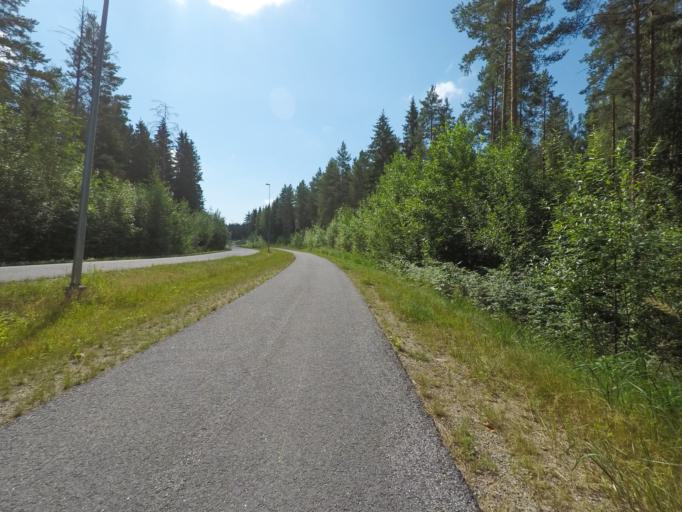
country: FI
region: Southern Savonia
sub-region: Mikkeli
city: Puumala
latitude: 61.5137
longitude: 28.1639
